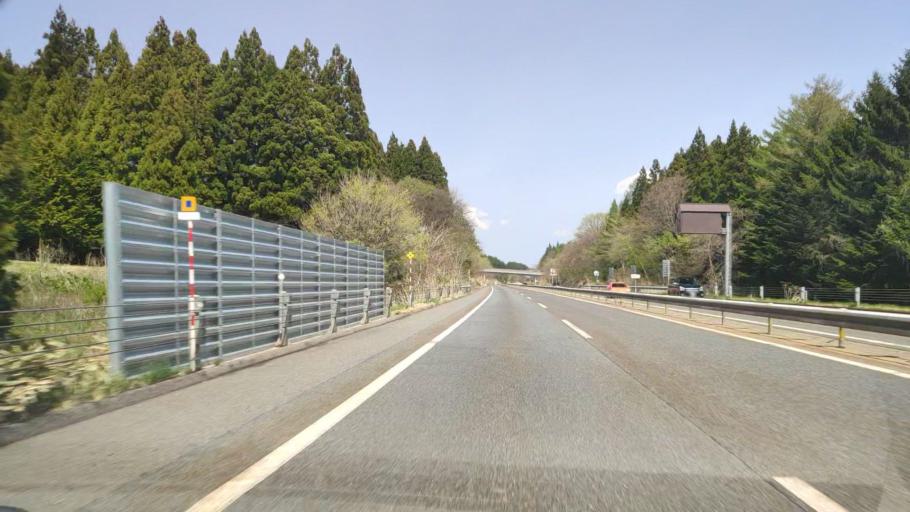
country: JP
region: Iwate
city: Ichinohe
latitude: 40.2575
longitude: 141.4022
